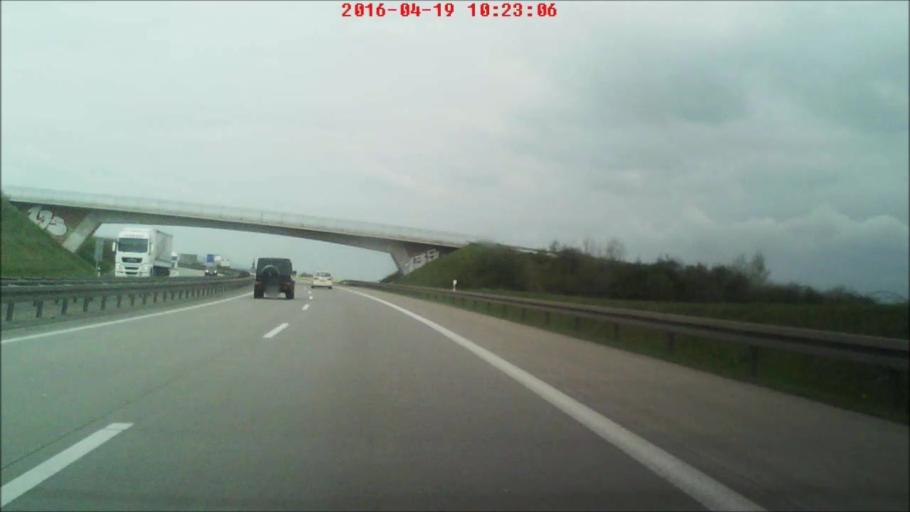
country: DE
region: Thuringia
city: Noda
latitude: 51.0349
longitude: 11.0105
